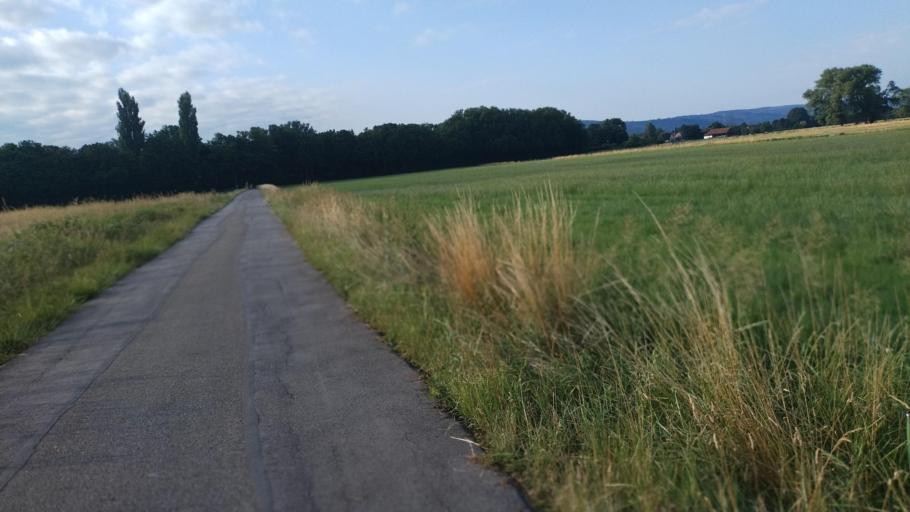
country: DE
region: Baden-Wuerttemberg
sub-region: Karlsruhe Region
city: Ettlingen
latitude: 48.9729
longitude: 8.3967
